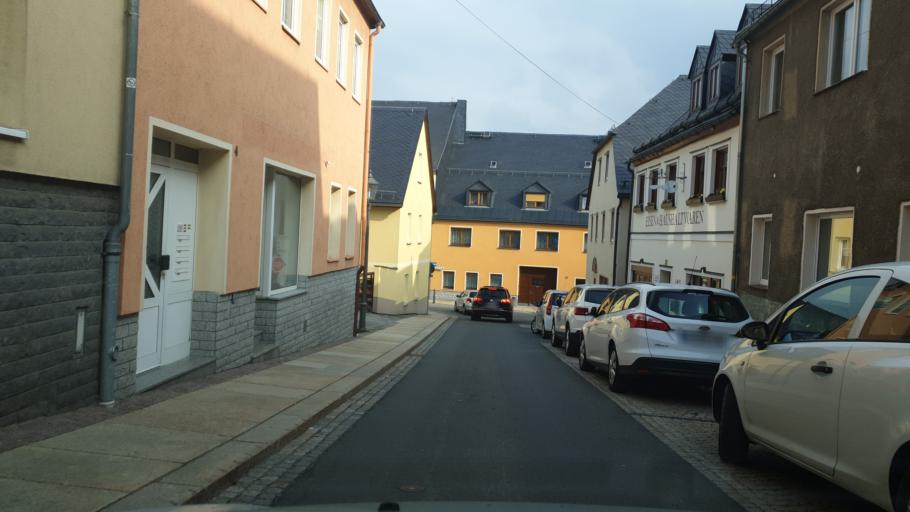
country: DE
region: Saxony
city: Lossnitz
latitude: 50.6204
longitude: 12.7293
